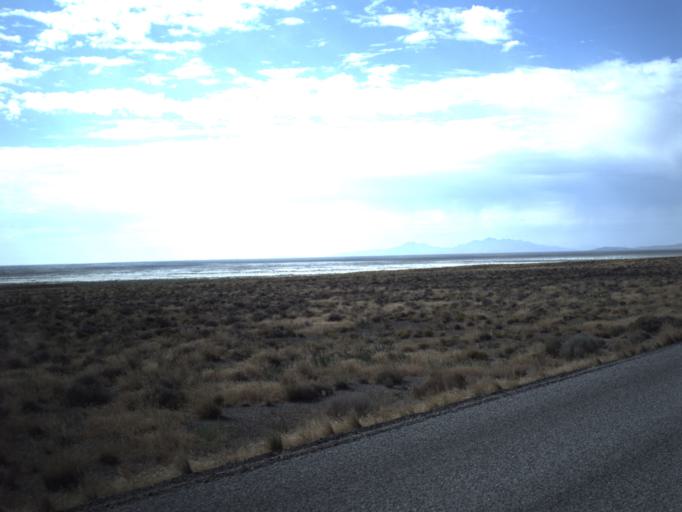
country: US
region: Utah
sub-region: Tooele County
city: Wendover
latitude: 41.4612
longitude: -113.6511
